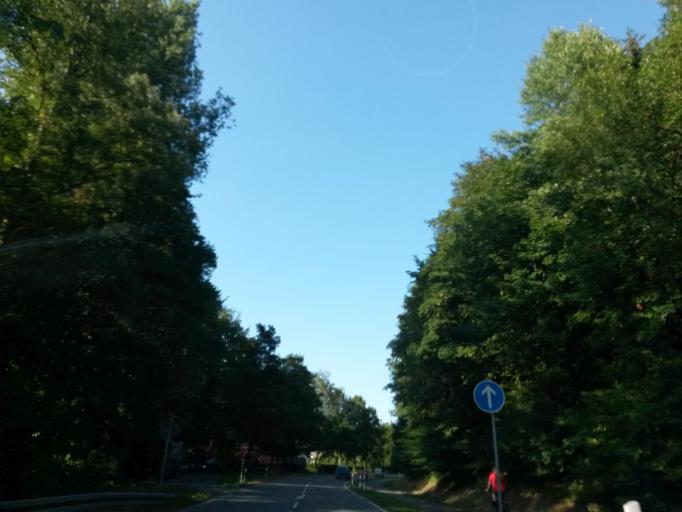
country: DE
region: North Rhine-Westphalia
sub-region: Regierungsbezirk Koln
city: Gummersbach
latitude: 51.0443
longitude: 7.6093
